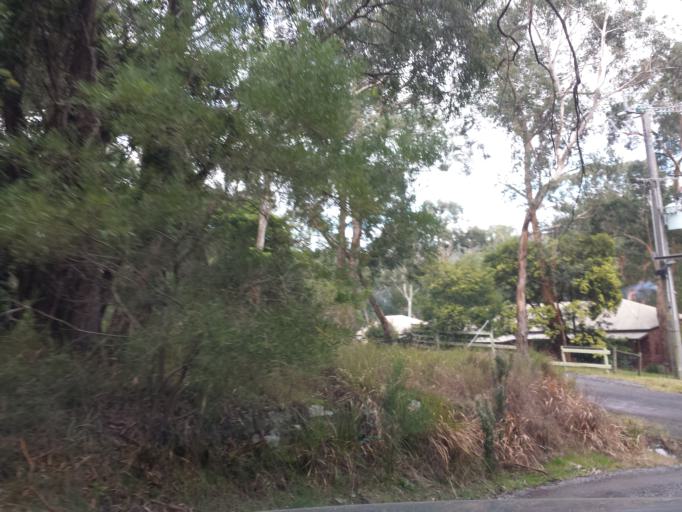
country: AU
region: Victoria
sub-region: Yarra Ranges
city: Belgrave Heights
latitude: -37.9206
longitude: 145.3609
